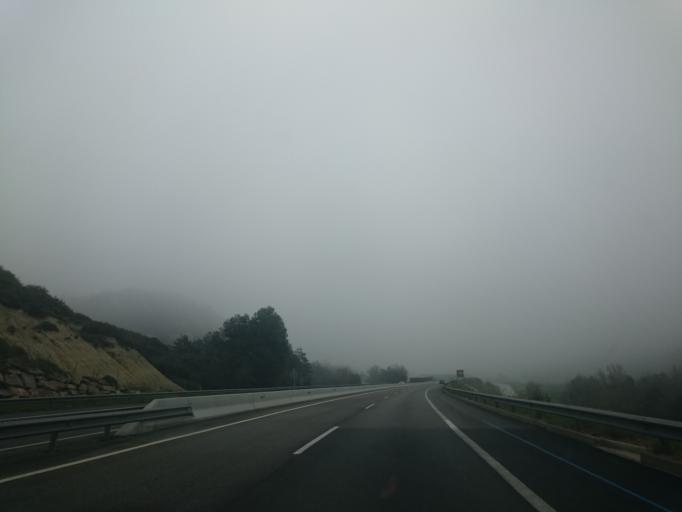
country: ES
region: Catalonia
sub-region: Provincia de Barcelona
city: Muntanyola
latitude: 41.9361
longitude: 2.1828
